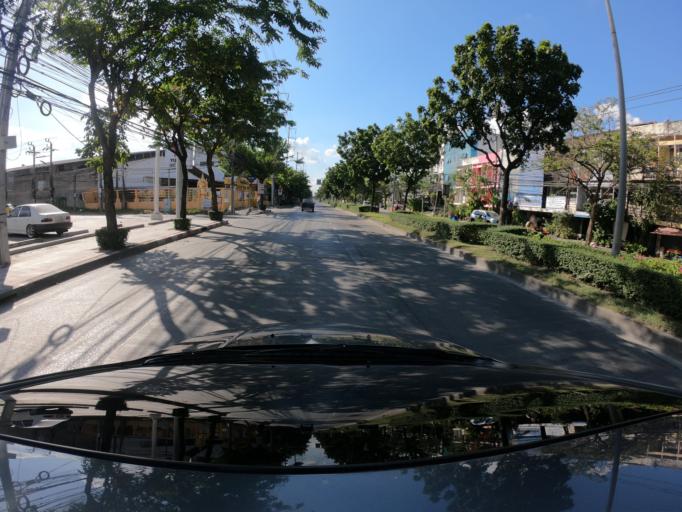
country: TH
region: Bangkok
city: Phra Khanong
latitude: 13.6748
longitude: 100.5977
